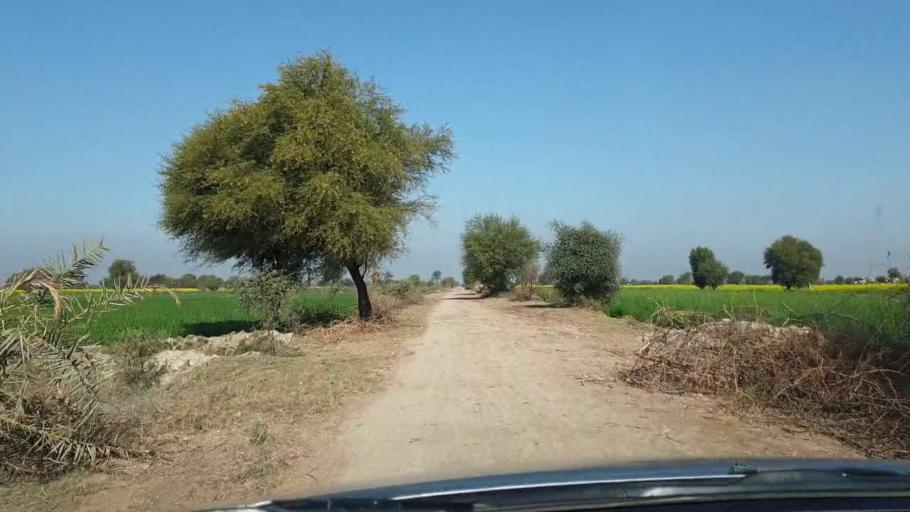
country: PK
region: Sindh
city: Jhol
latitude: 25.8834
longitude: 68.9053
